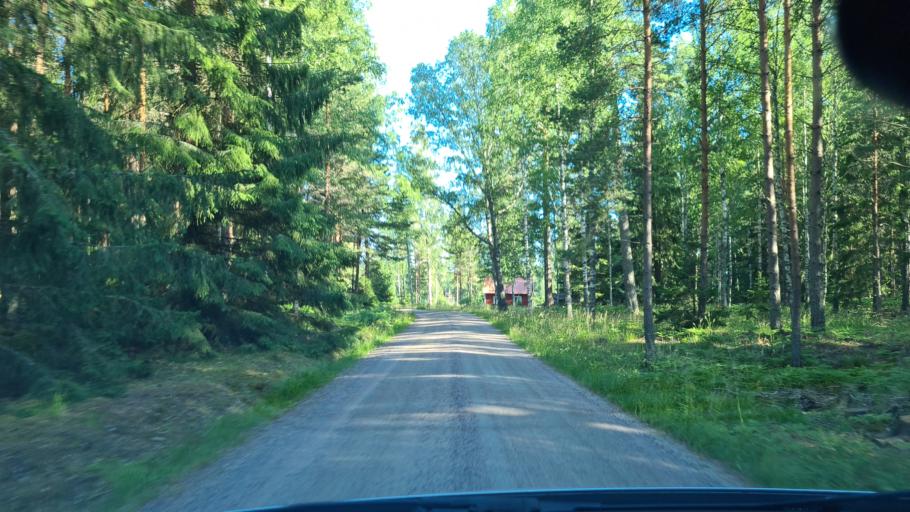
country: SE
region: Soedermanland
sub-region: Nykopings Kommun
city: Stigtomta
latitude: 58.9169
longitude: 16.9133
